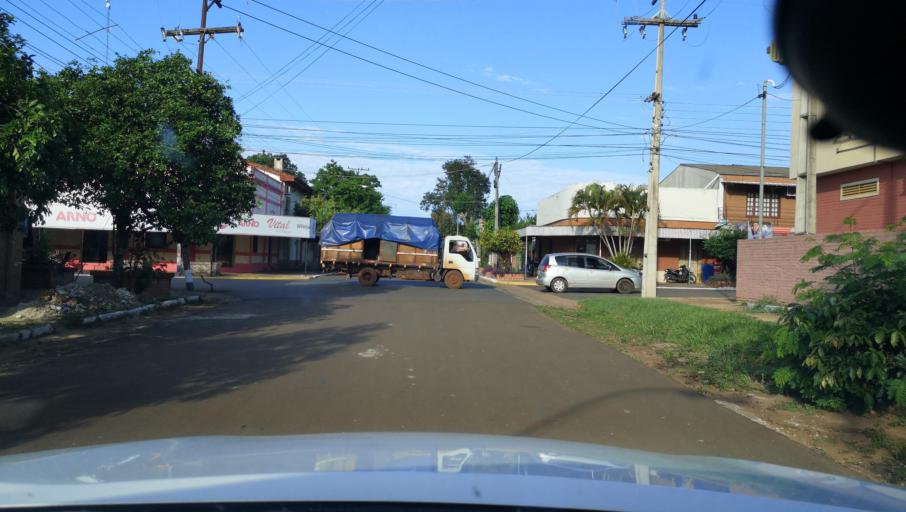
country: PY
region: Itapua
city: Carmen del Parana
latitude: -27.1602
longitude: -56.2394
